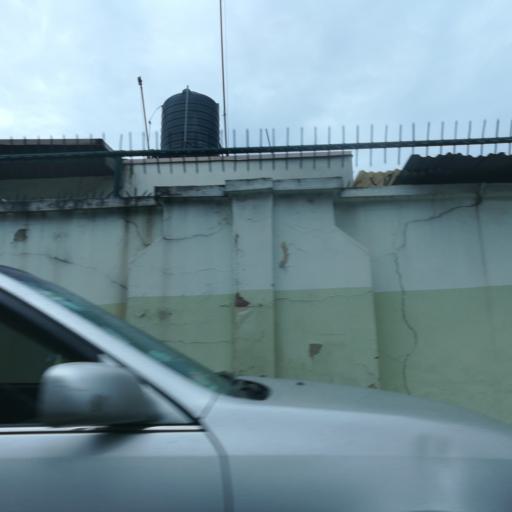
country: NG
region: Lagos
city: Makoko
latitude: 6.5027
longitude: 3.3763
